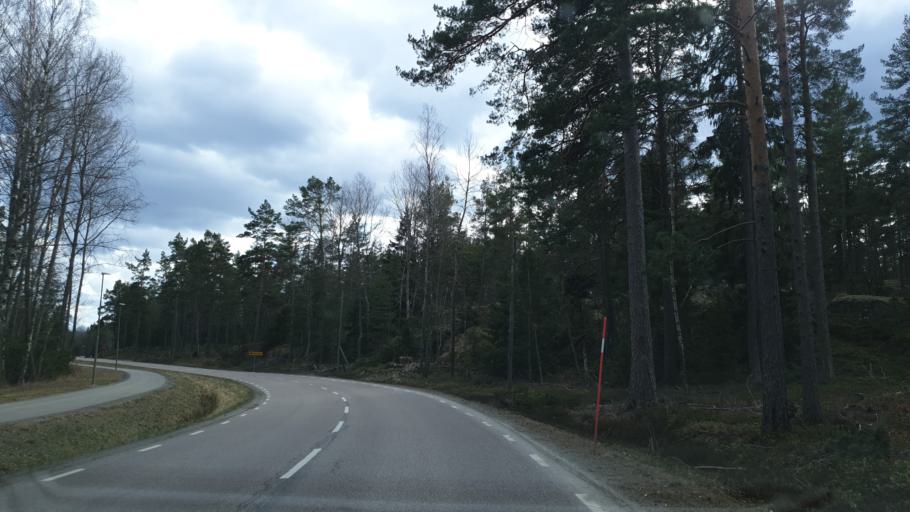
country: SE
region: Stockholm
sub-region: Varmdo Kommun
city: Mortnas
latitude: 59.2756
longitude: 18.4247
